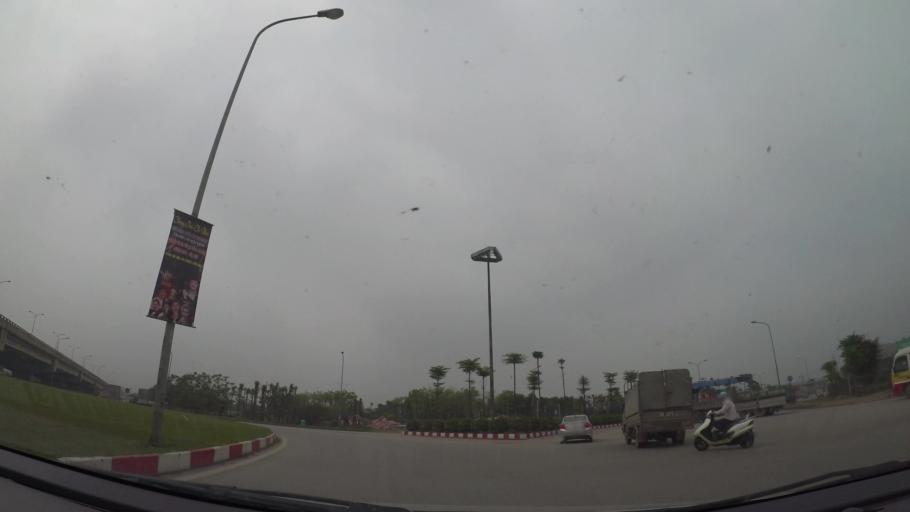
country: VN
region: Ha Noi
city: Tay Ho
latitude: 21.1256
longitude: 105.7810
